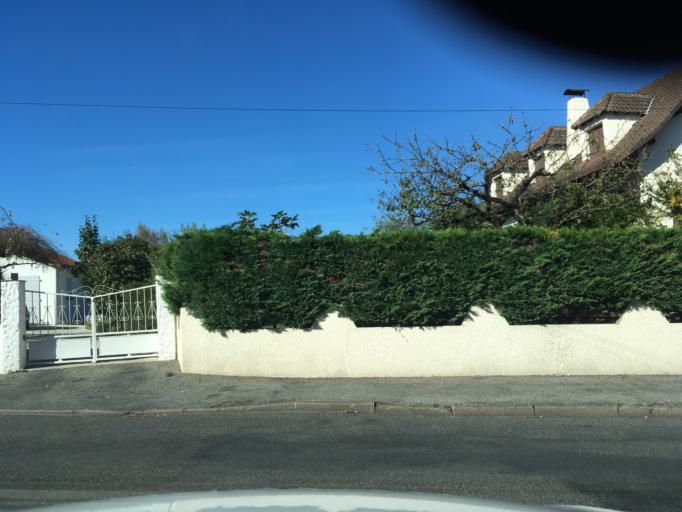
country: FR
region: Aquitaine
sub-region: Departement des Pyrenees-Atlantiques
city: Pau
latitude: 43.3139
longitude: -0.3403
